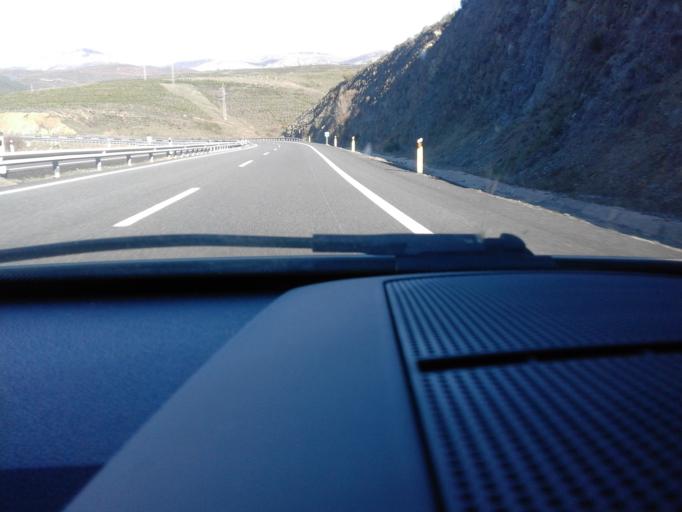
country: ES
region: Castille and Leon
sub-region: Provincia de Leon
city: Carrocera
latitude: 42.7637
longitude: -5.7763
